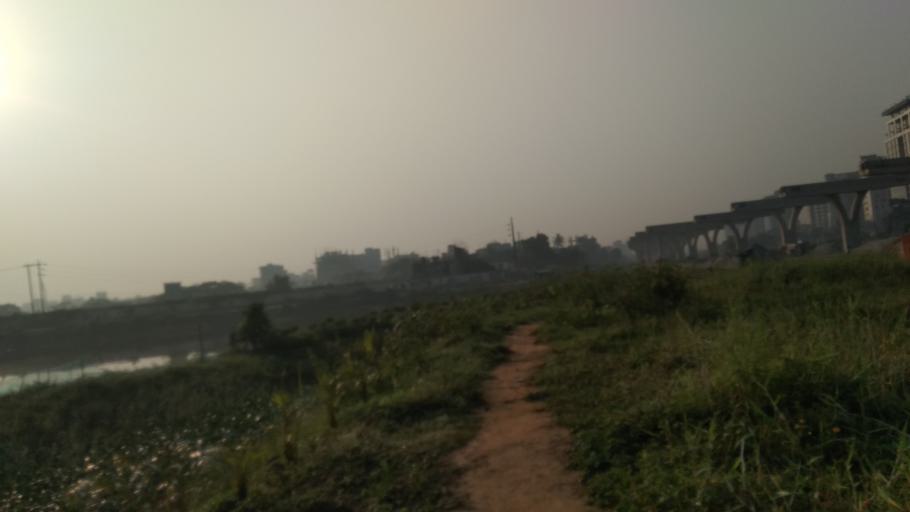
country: BD
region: Dhaka
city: Tungi
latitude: 23.8395
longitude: 90.4189
